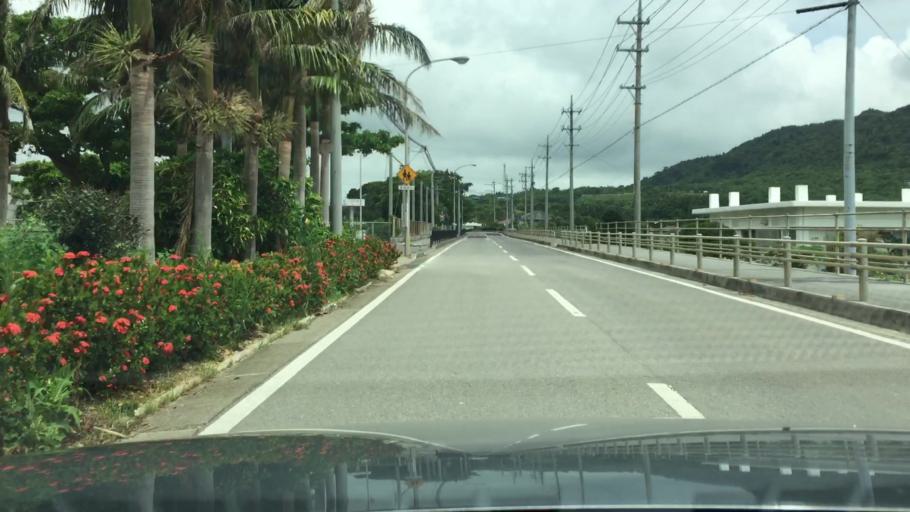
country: JP
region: Okinawa
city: Ishigaki
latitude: 24.3934
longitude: 124.1605
